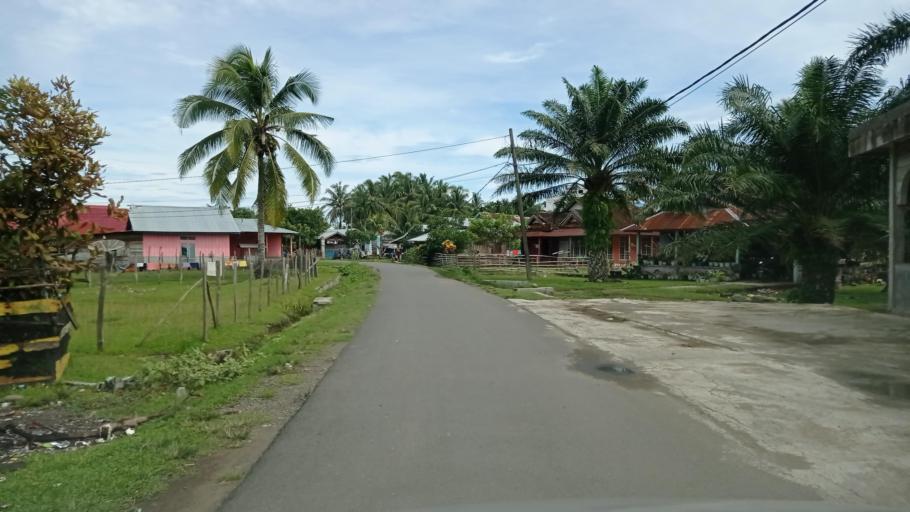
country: ID
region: Bengkulu
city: Ipuh
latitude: -2.5876
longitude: 101.1148
